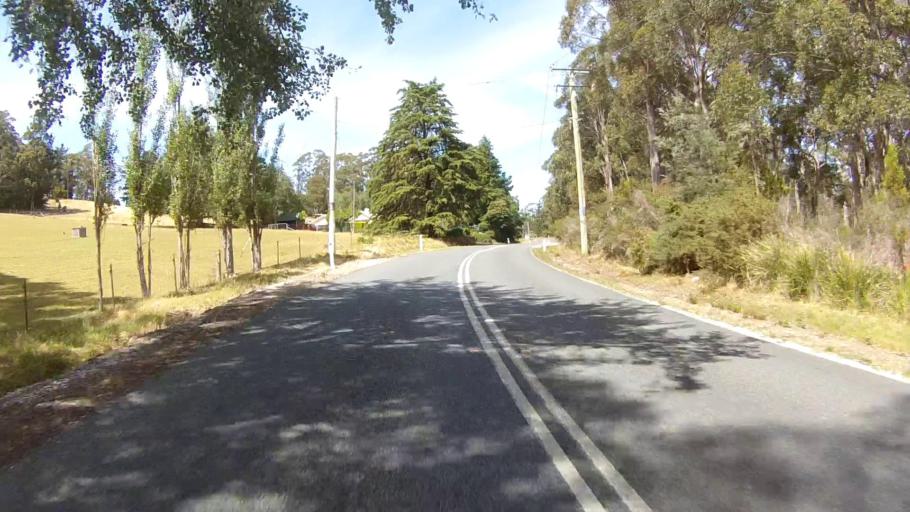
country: AU
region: Tasmania
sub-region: Huon Valley
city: Cygnet
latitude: -43.2257
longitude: 147.1279
